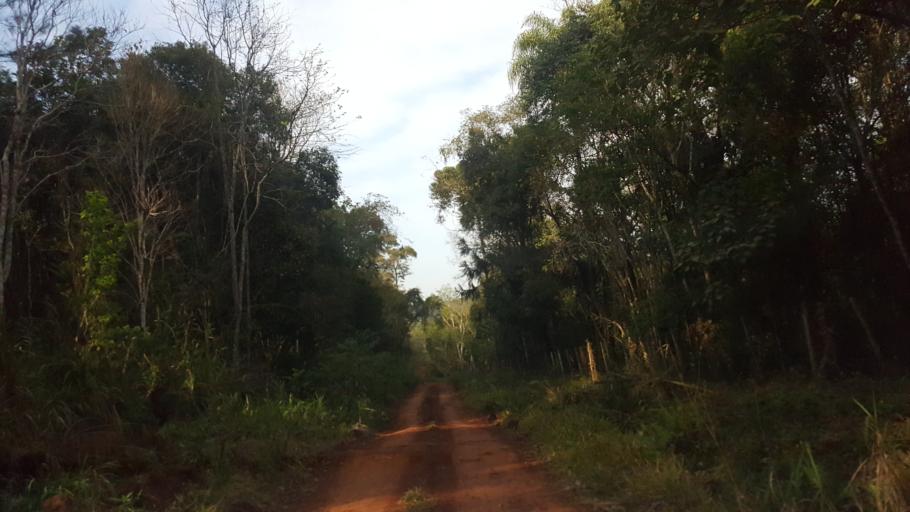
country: AR
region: Misiones
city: Capiovi
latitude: -26.8951
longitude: -55.1072
